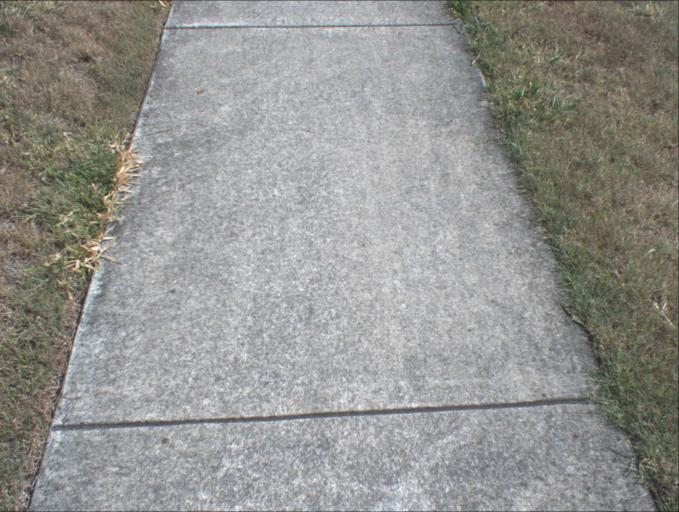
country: AU
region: Queensland
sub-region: Logan
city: Windaroo
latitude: -27.7231
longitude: 153.1878
